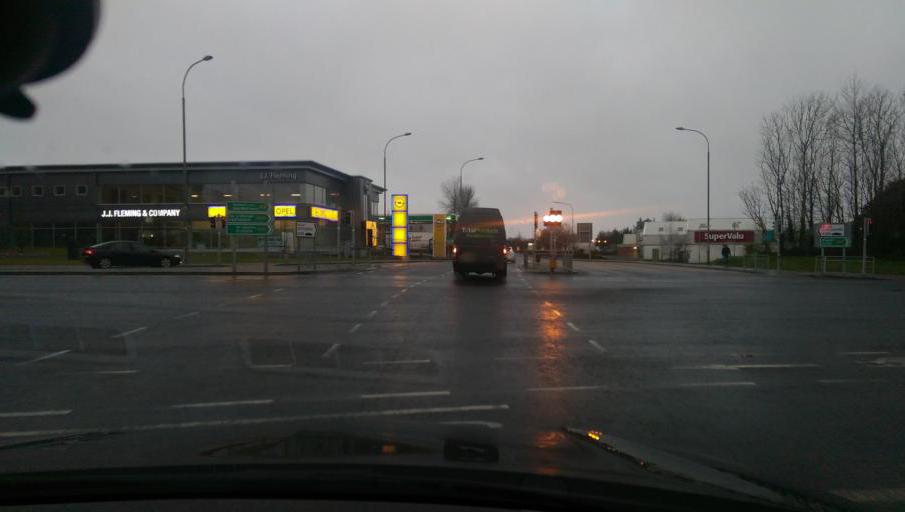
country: IE
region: Connaught
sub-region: County Galway
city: Gaillimh
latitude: 53.2909
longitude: -9.0198
